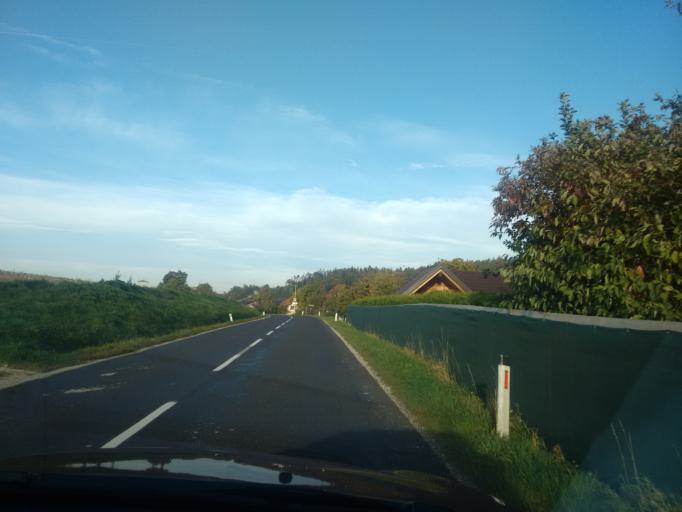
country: AT
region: Upper Austria
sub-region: Politischer Bezirk Vocklabruck
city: Niederthalheim
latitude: 48.1313
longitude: 13.7239
